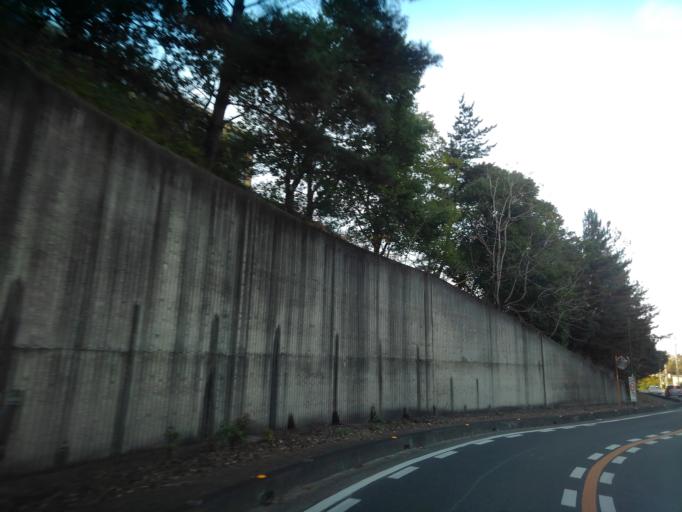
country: JP
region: Saitama
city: Hanno
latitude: 35.8322
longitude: 139.3362
